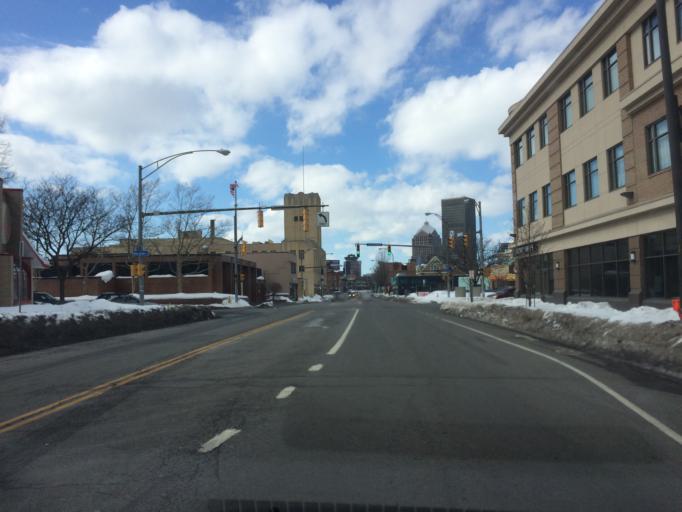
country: US
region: New York
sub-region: Monroe County
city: Rochester
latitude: 43.1486
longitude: -77.5971
